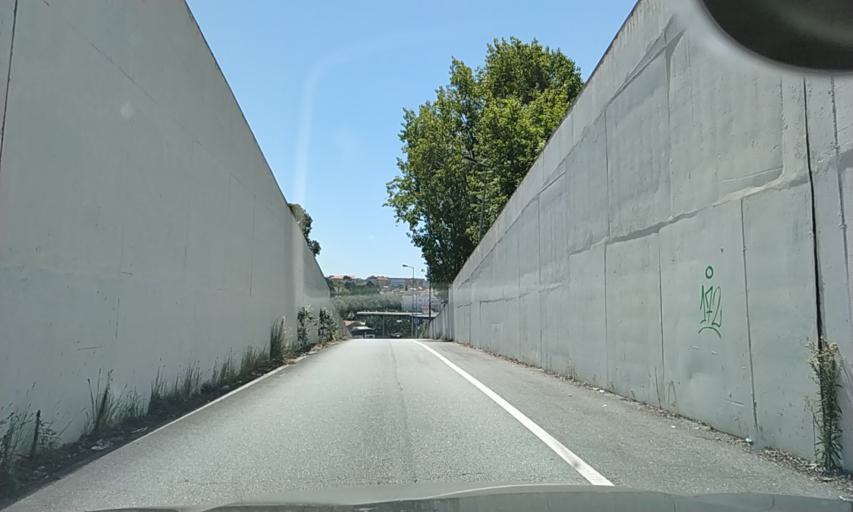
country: PT
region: Porto
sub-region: Vila Nova de Gaia
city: Canidelo
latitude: 41.1418
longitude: -8.6420
